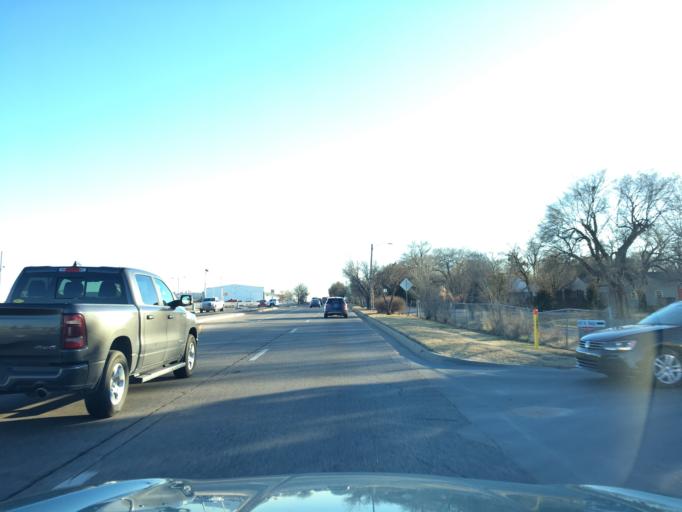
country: US
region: Kansas
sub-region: Sedgwick County
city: Bellaire
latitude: 37.6926
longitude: -97.2263
